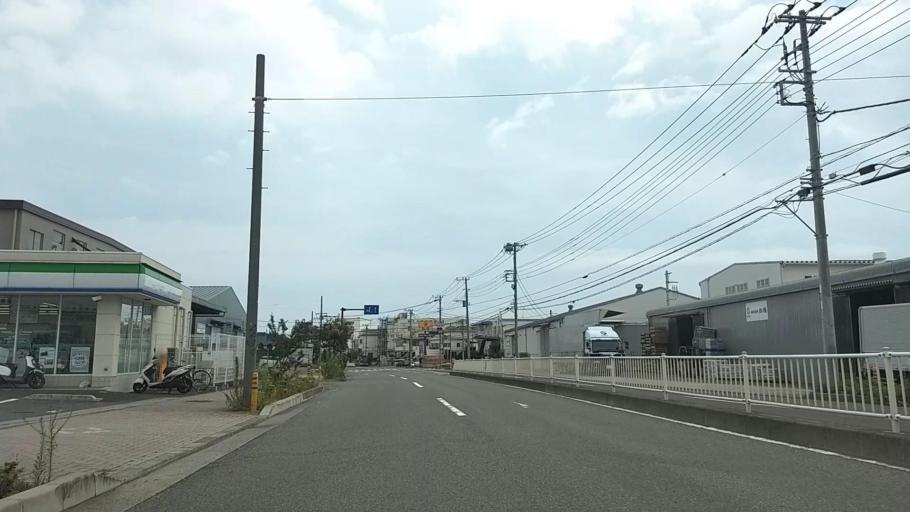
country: JP
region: Kanagawa
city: Minami-rinkan
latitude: 35.4536
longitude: 139.4177
